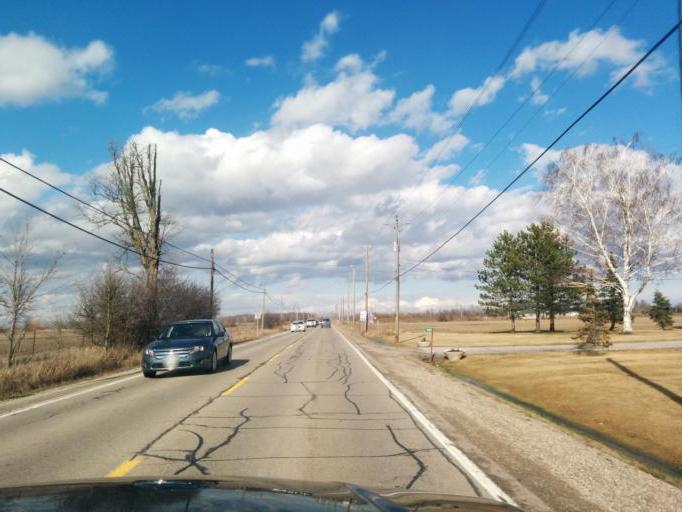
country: CA
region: Ontario
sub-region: Halton
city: Milton
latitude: 43.5379
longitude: -79.7784
